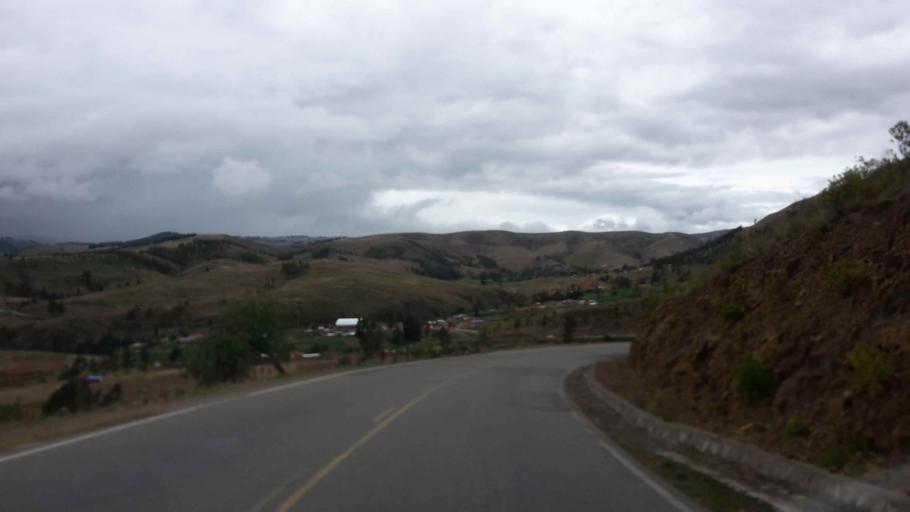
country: BO
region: Cochabamba
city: Punata
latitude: -17.4819
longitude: -65.7748
